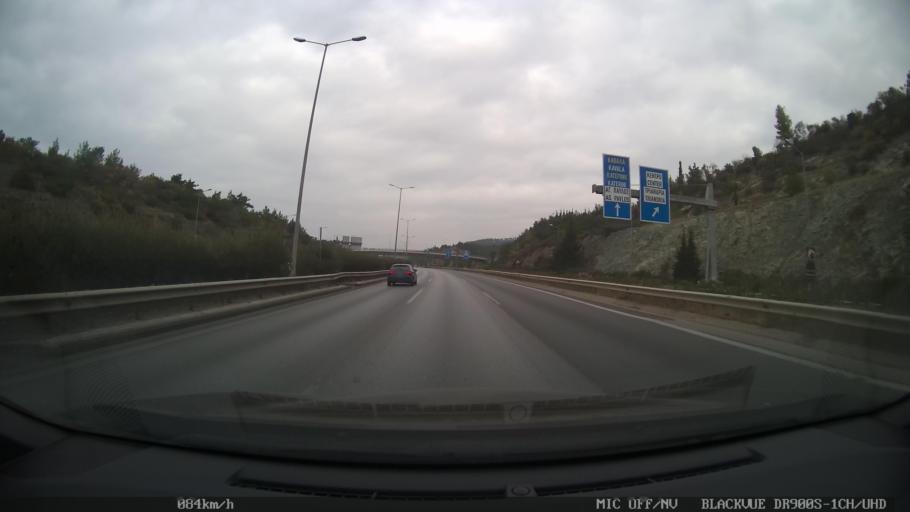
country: GR
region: Central Macedonia
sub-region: Nomos Thessalonikis
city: Triandria
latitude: 40.6241
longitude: 22.9811
